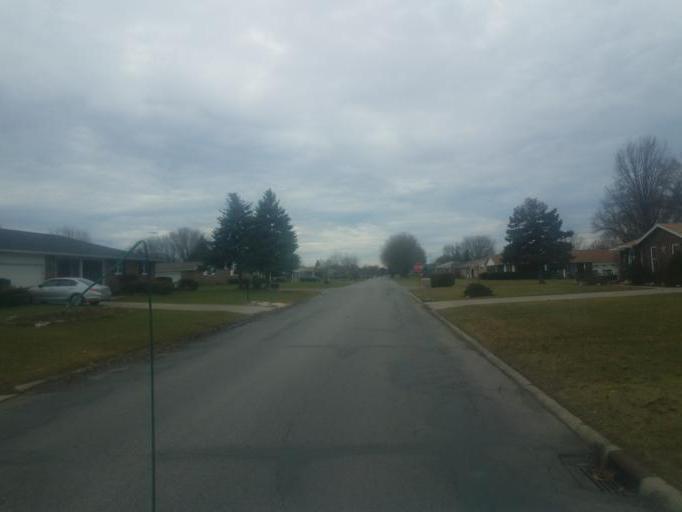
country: US
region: Ohio
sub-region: Marion County
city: Marion
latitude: 40.5776
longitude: -83.0802
